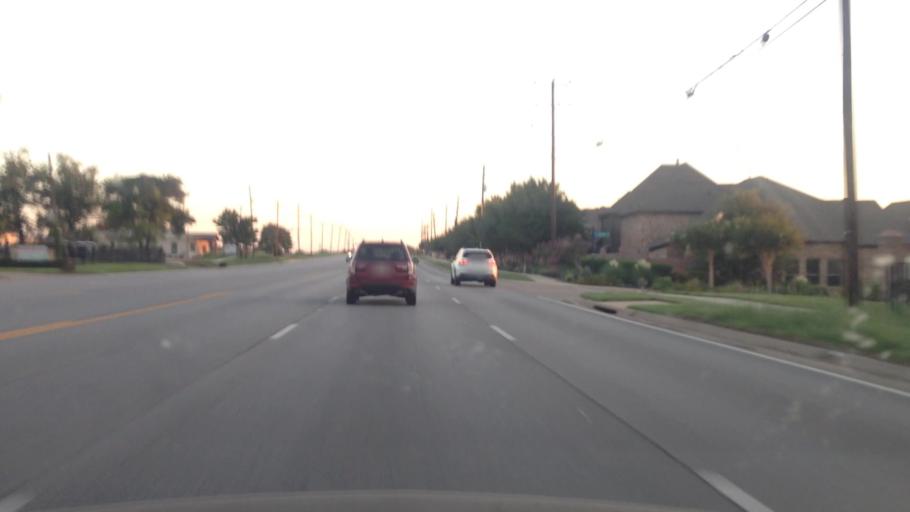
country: US
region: Texas
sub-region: Tarrant County
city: Colleyville
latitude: 32.8870
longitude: -97.2035
